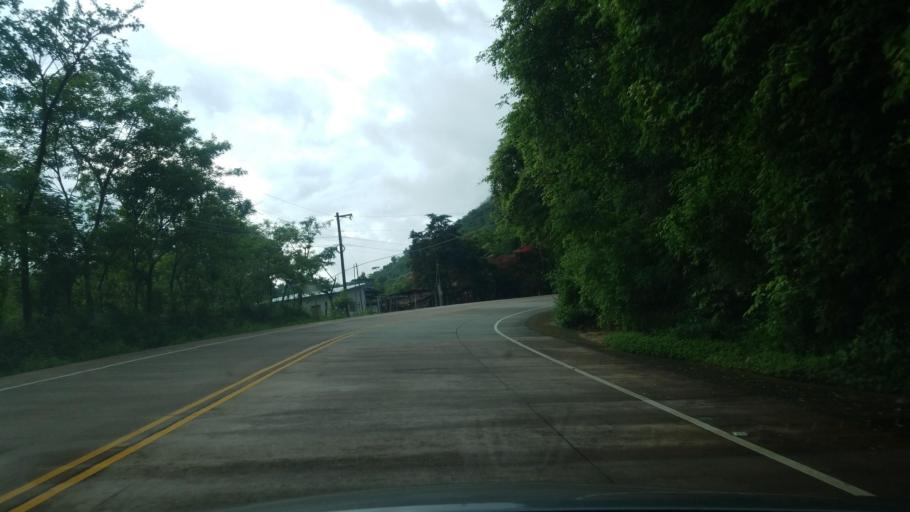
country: HN
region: Copan
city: Copan
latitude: 14.8434
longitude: -89.1893
